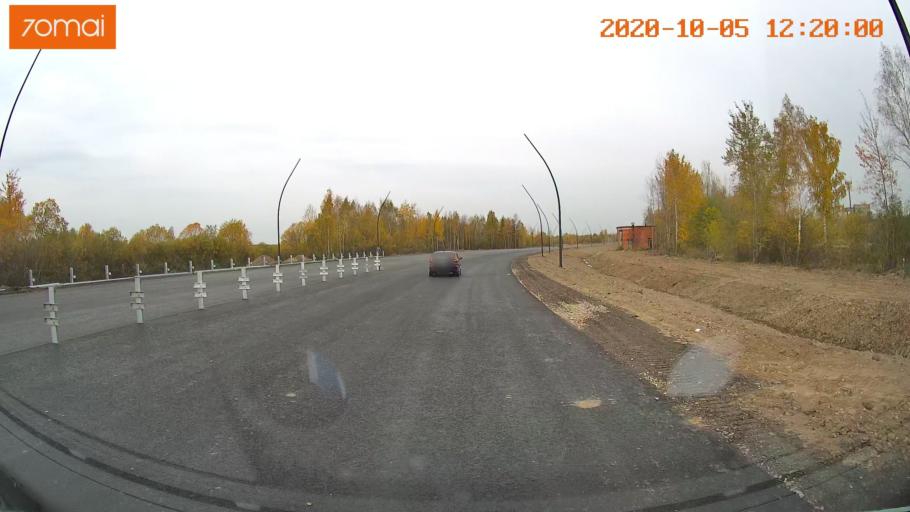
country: RU
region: Ivanovo
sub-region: Gorod Ivanovo
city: Ivanovo
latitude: 56.9589
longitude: 40.9319
